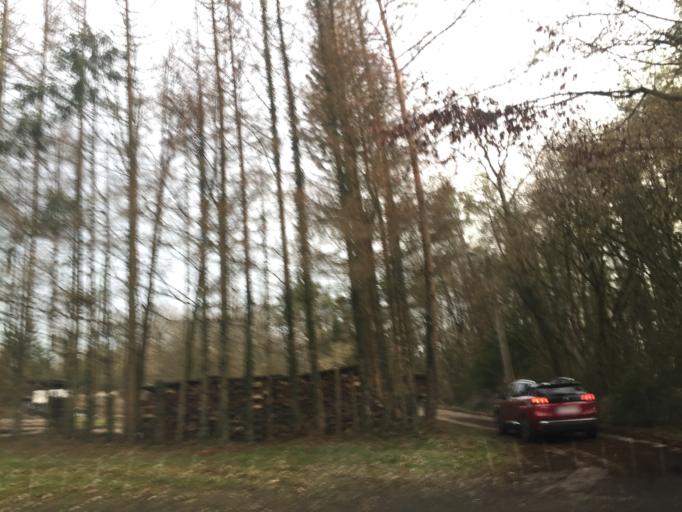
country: BE
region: Wallonia
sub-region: Province du Luxembourg
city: Hotton
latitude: 50.3026
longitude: 5.4950
